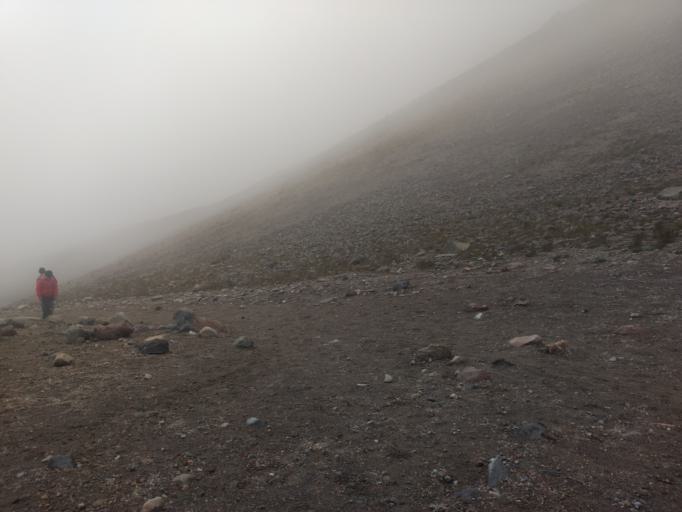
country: MX
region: Mexico
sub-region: Tenango del Valle
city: Santa Cruz Pueblo Nuevo (Pueblo Nuevo)
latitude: 19.1125
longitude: -99.7522
